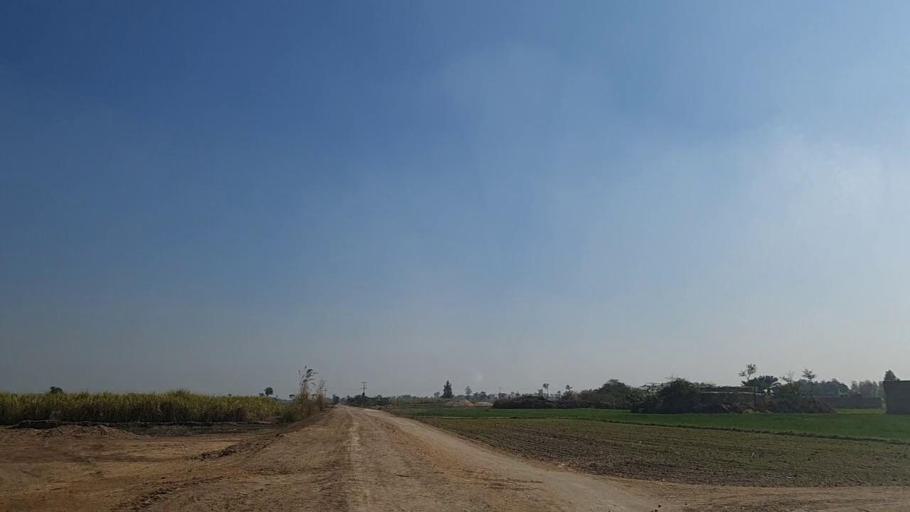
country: PK
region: Sindh
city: Daur
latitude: 26.4820
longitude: 68.3356
